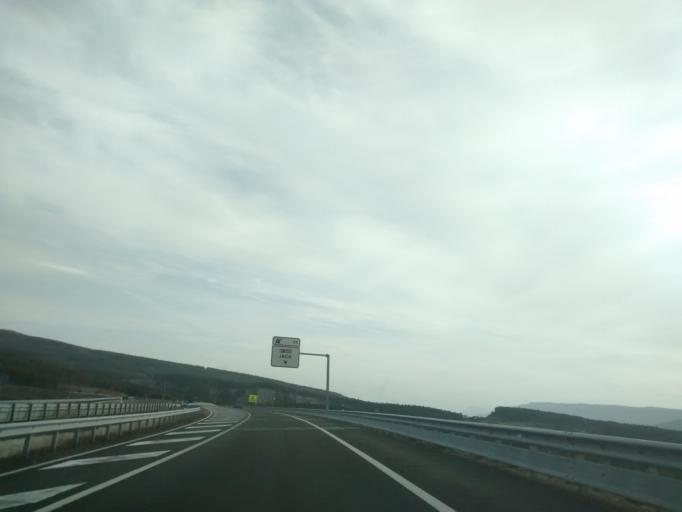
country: ES
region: Aragon
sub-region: Provincia de Zaragoza
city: Undues de Lerda
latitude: 42.6222
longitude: -1.1161
